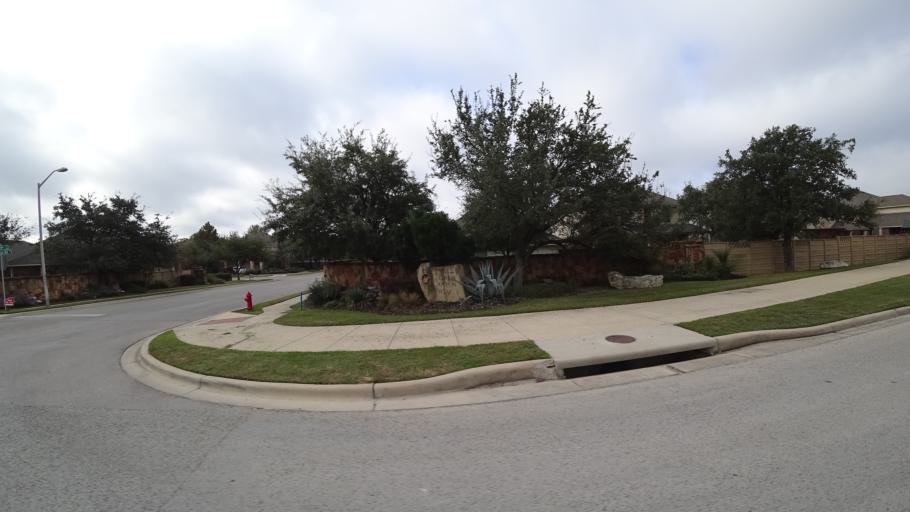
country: US
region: Texas
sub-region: Williamson County
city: Cedar Park
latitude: 30.4882
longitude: -97.8586
